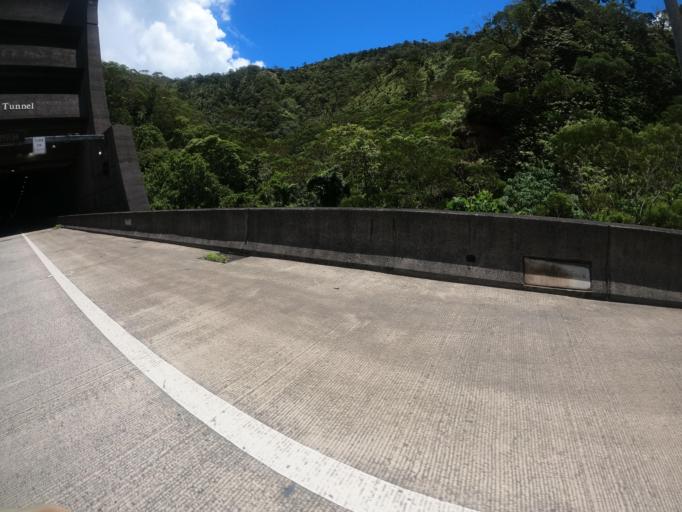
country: US
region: Hawaii
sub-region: Honolulu County
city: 'Ahuimanu
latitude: 21.4046
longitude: -157.8508
